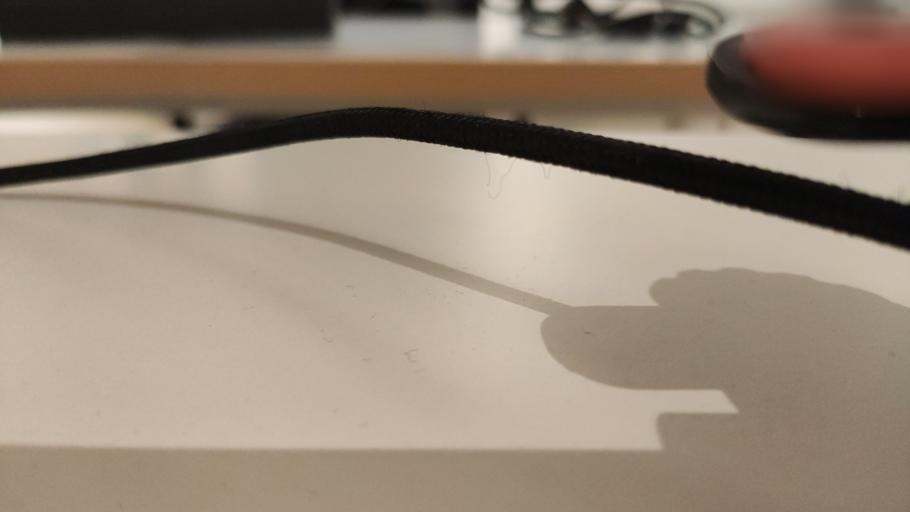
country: RU
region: Moskovskaya
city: Dorokhovo
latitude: 55.5291
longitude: 36.3577
